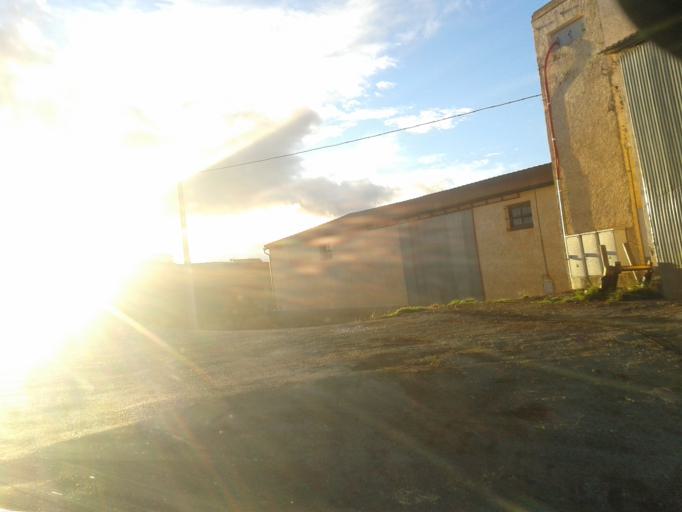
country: ES
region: Aragon
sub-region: Provincia de Teruel
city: Ferreruela de Huerva
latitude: 41.0625
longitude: -1.2343
